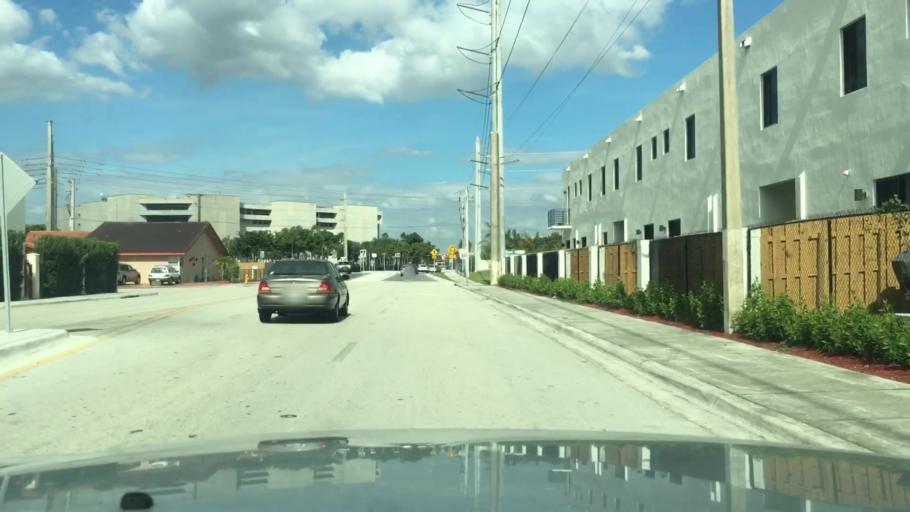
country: US
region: Florida
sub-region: Miami-Dade County
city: Fountainebleau
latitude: 25.7644
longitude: -80.3442
